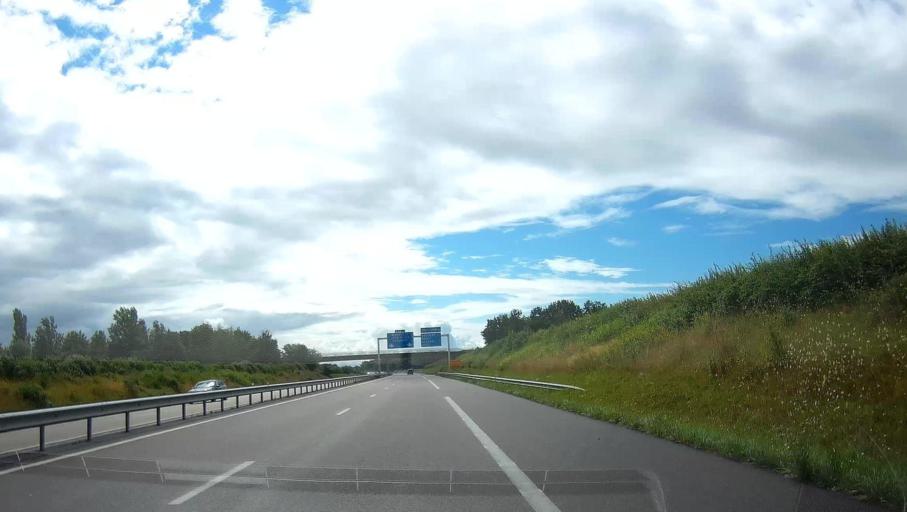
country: FR
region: Champagne-Ardenne
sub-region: Departement de l'Aube
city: Verrieres
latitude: 48.2429
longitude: 4.1703
